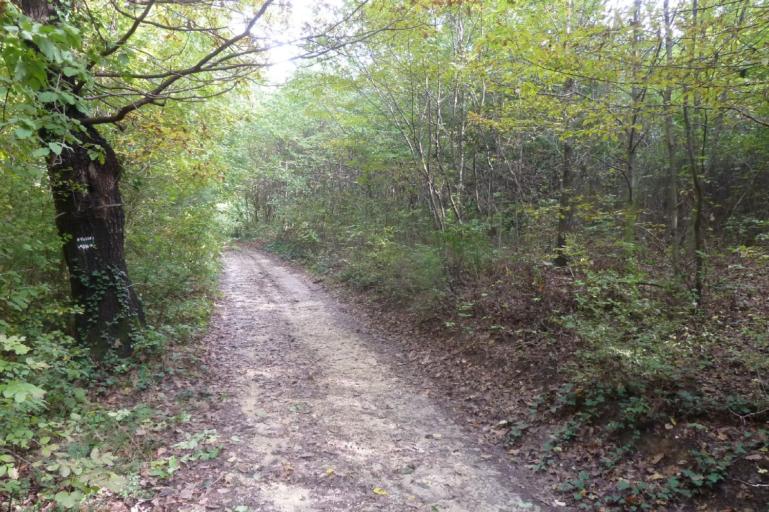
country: HU
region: Pest
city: Pilisborosjeno
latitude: 47.5780
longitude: 18.9706
